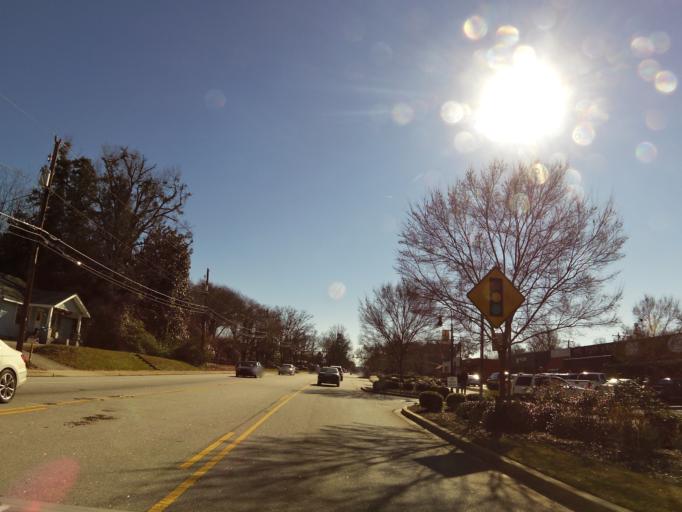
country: US
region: South Carolina
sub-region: Greenville County
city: Travelers Rest
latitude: 34.9623
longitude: -82.4407
